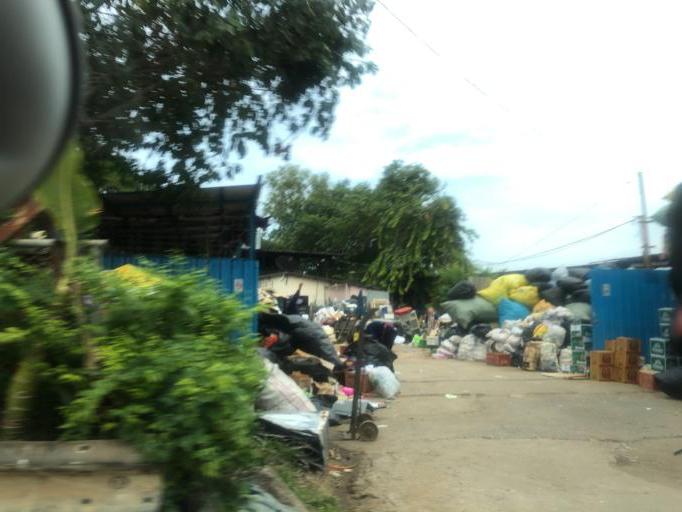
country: TH
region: Bangkok
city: Don Mueang
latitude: 13.9671
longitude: 100.6081
